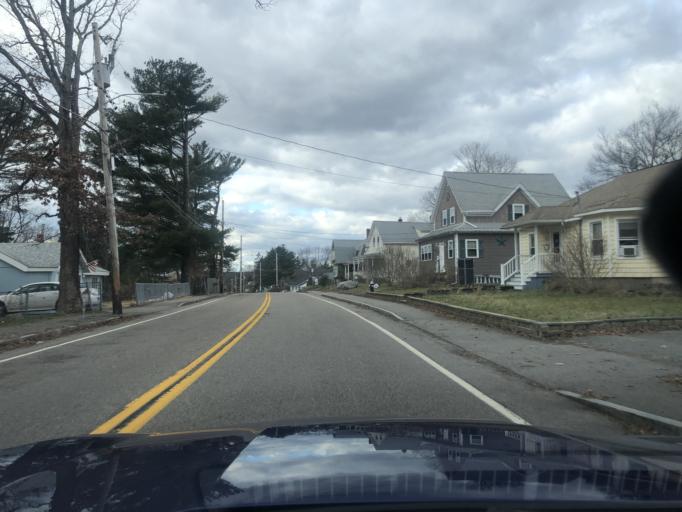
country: US
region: Massachusetts
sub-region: Plymouth County
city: Brockton
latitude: 42.1089
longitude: -71.0100
